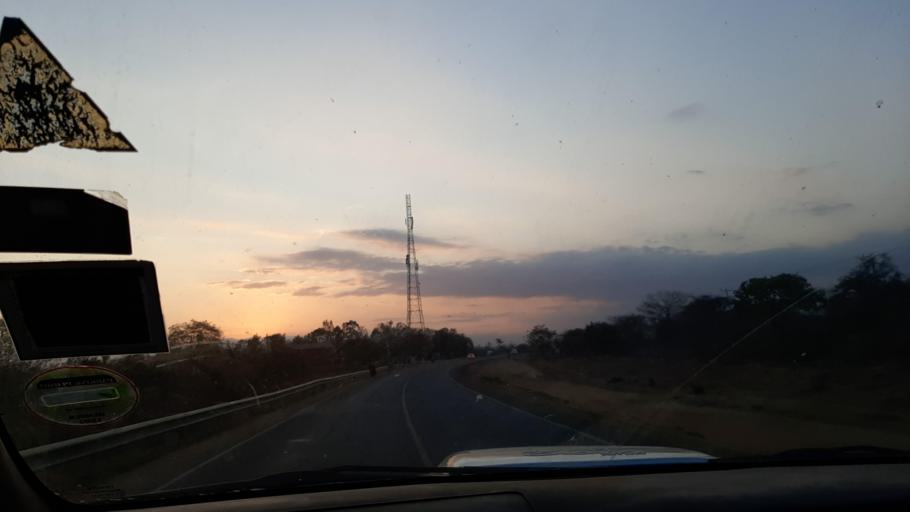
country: KE
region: Machakos
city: Kangundo
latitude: -1.4126
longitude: 37.5507
